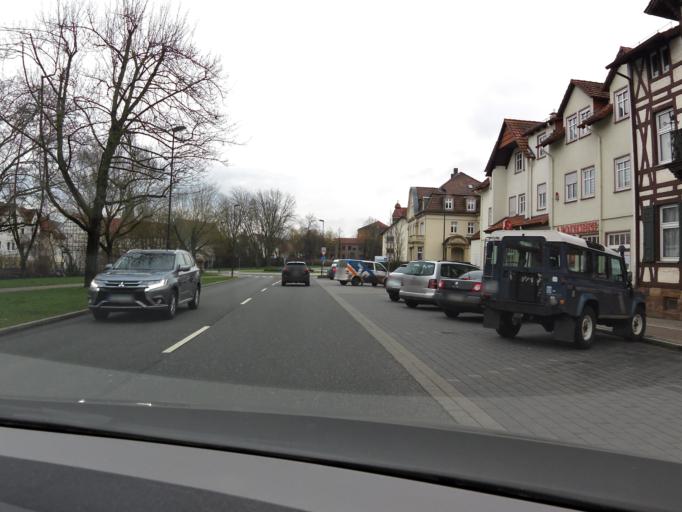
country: DE
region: Hesse
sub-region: Regierungsbezirk Kassel
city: Eschwege
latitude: 51.1858
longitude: 10.0534
